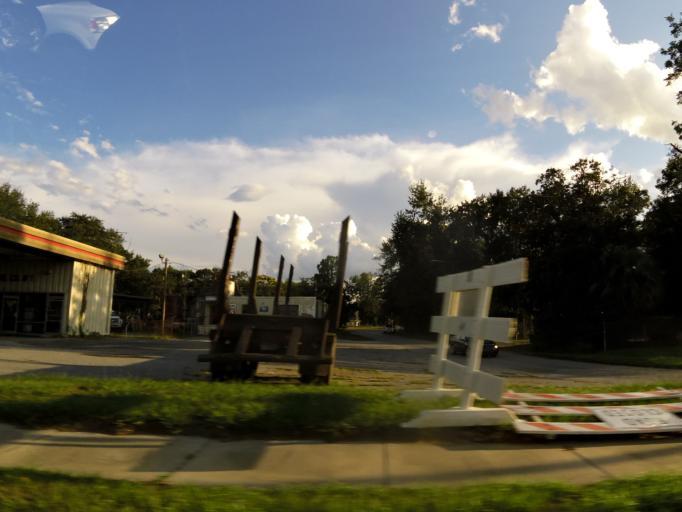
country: US
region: Georgia
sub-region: Lowndes County
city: Valdosta
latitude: 30.8231
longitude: -83.2988
